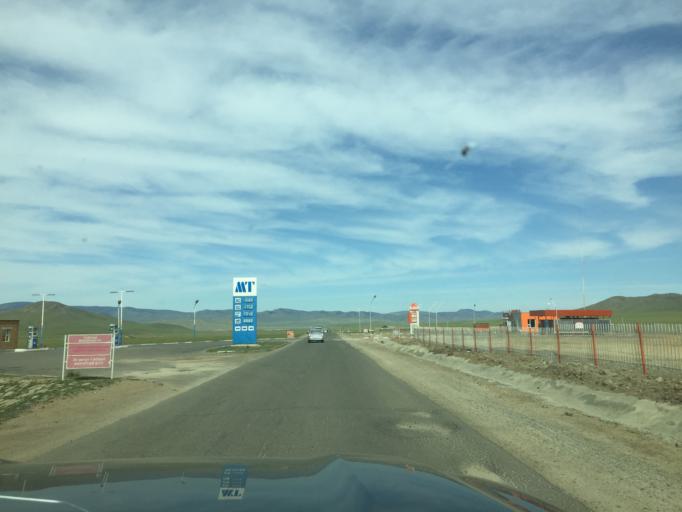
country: MN
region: Central Aimak
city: Ihsueuej
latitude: 48.2287
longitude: 106.2859
